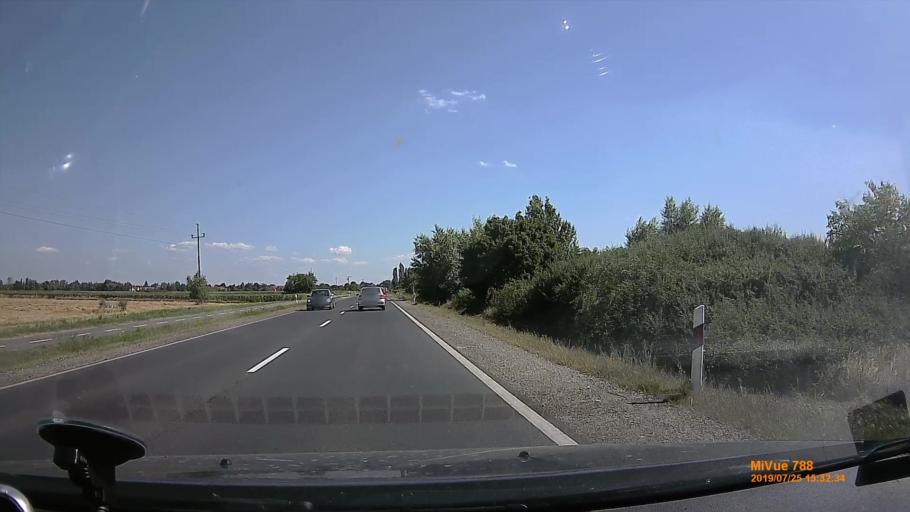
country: HU
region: Borsod-Abauj-Zemplen
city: Malyi
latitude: 48.0050
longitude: 20.8292
